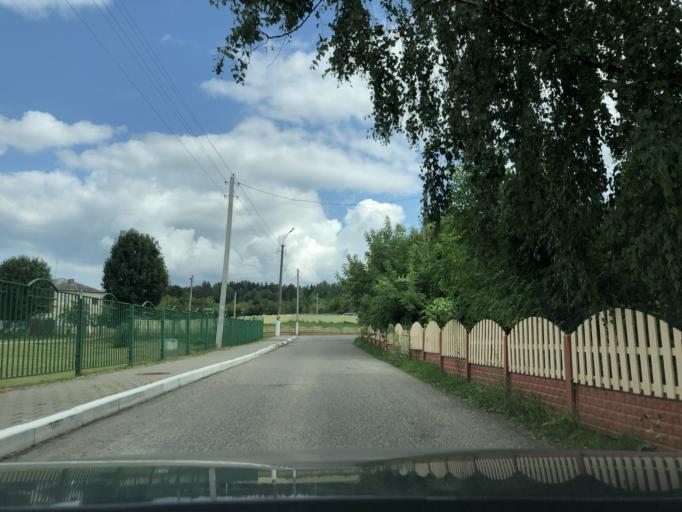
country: BY
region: Minsk
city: Lahoysk
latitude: 54.2054
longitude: 27.8522
